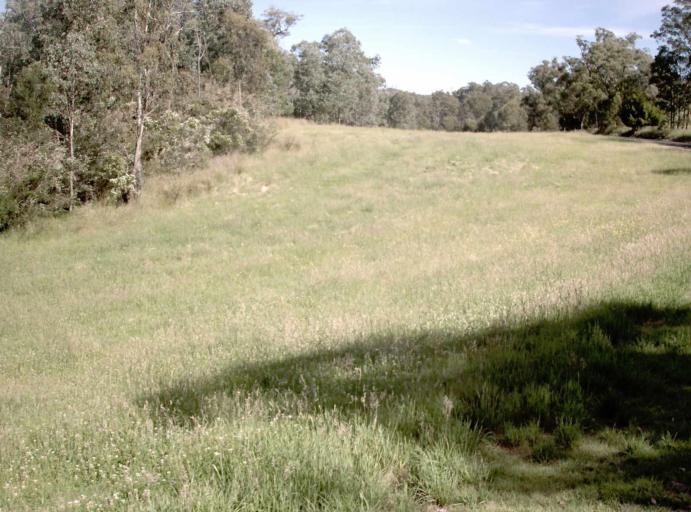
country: AU
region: Victoria
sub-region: East Gippsland
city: Lakes Entrance
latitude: -37.4851
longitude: 148.1280
